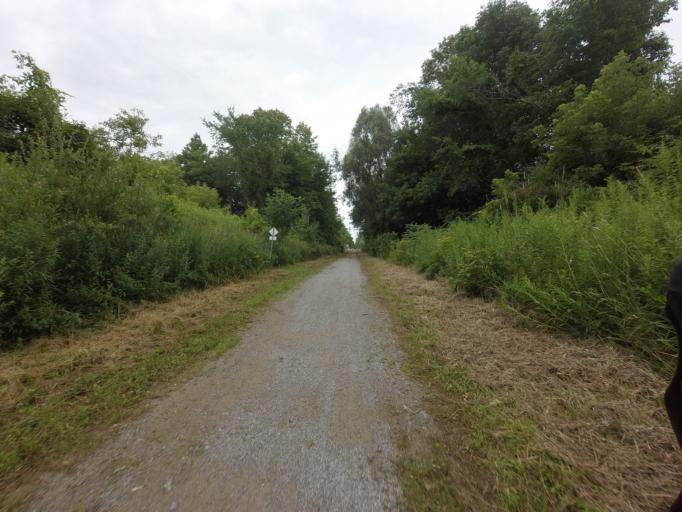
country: CA
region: Ontario
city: Ottawa
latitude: 45.2762
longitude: -75.6249
